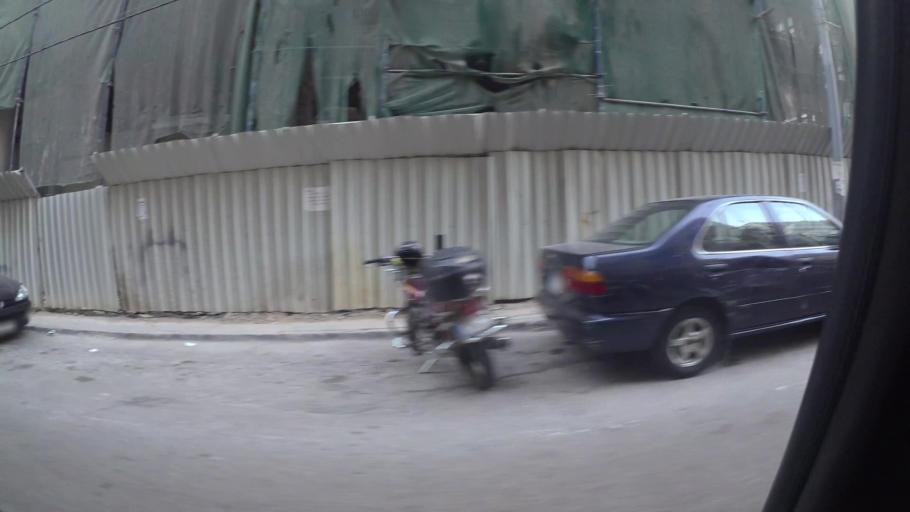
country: LB
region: Beyrouth
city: Ra's Bayrut
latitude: 33.8944
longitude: 35.4774
